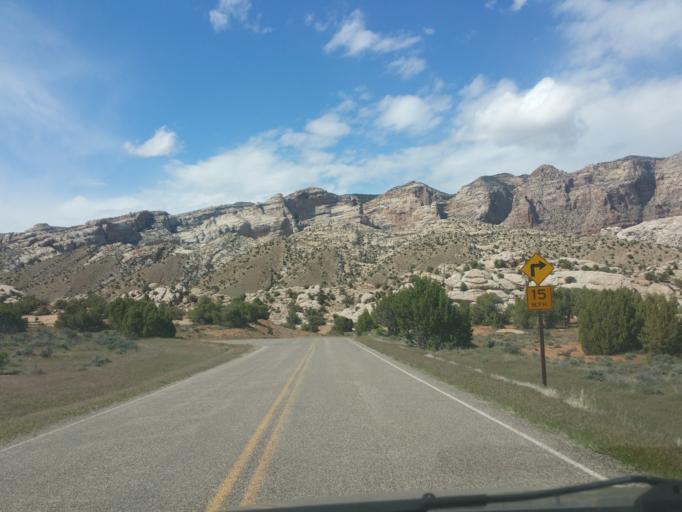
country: US
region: Utah
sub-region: Uintah County
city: Naples
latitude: 40.4405
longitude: -109.2606
